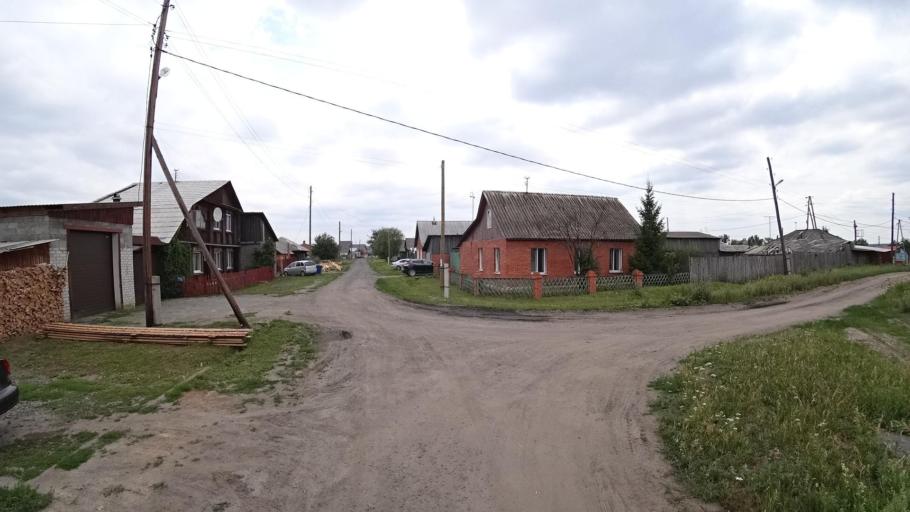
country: RU
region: Sverdlovsk
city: Kamyshlov
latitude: 56.8528
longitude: 62.6723
